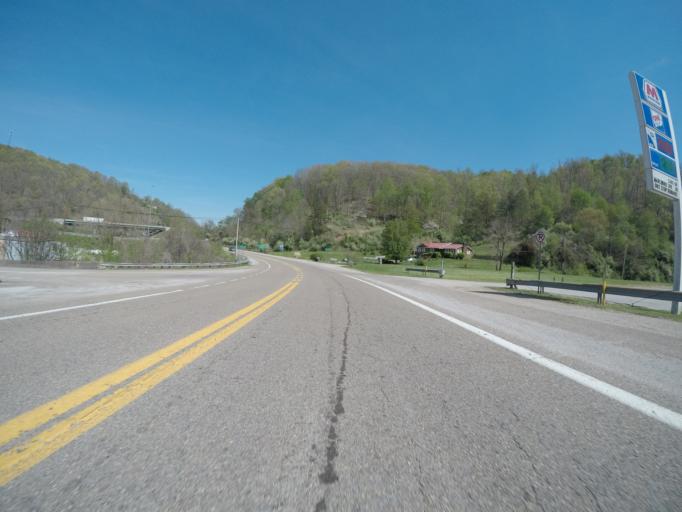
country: US
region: West Virginia
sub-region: Kanawha County
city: Charleston
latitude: 38.4120
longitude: -81.6335
